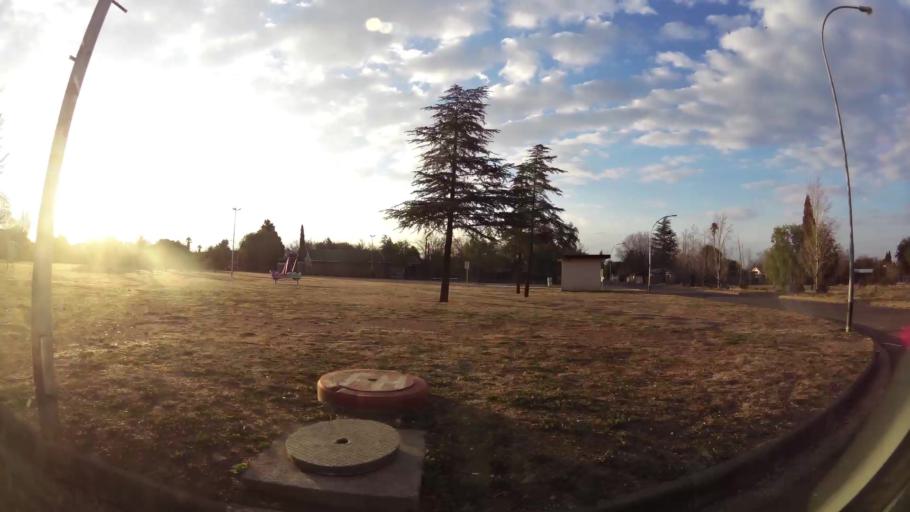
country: ZA
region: Orange Free State
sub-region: Mangaung Metropolitan Municipality
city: Bloemfontein
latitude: -29.1365
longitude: 26.1794
